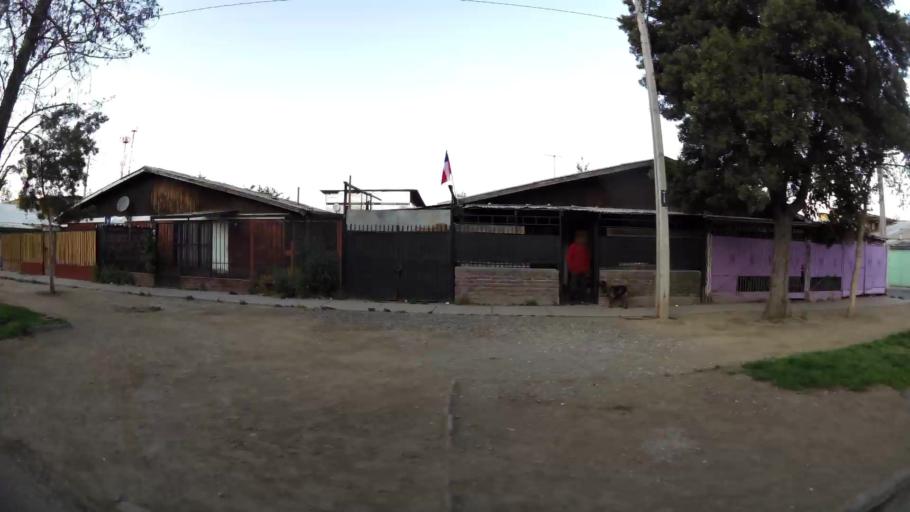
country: CL
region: Santiago Metropolitan
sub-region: Provincia de Santiago
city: Santiago
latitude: -33.3721
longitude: -70.6336
